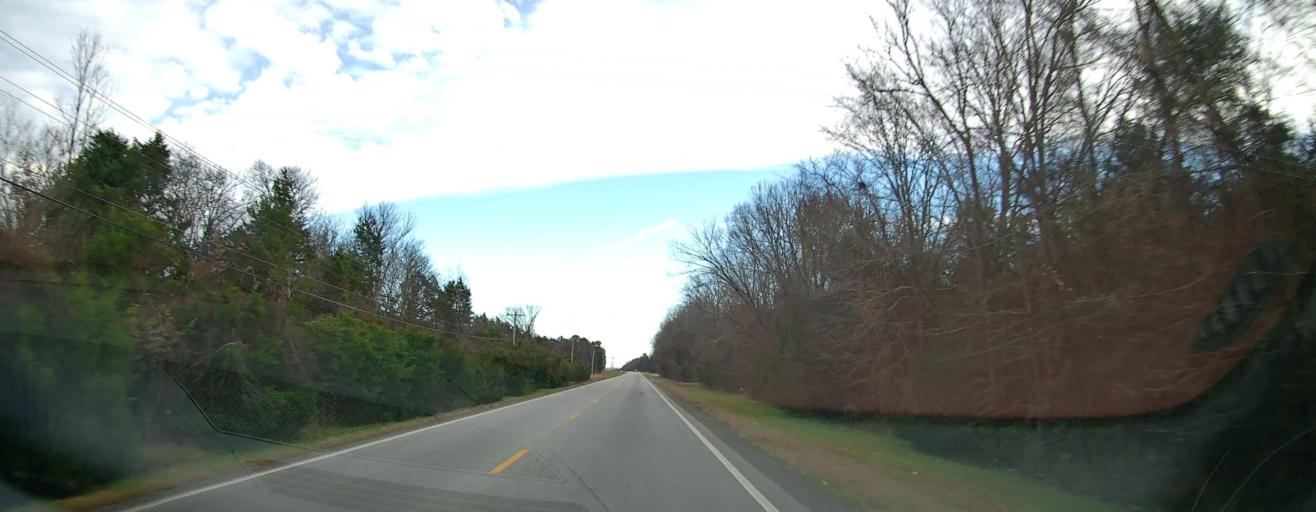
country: US
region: Alabama
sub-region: Morgan County
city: Priceville
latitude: 34.4404
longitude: -86.7473
